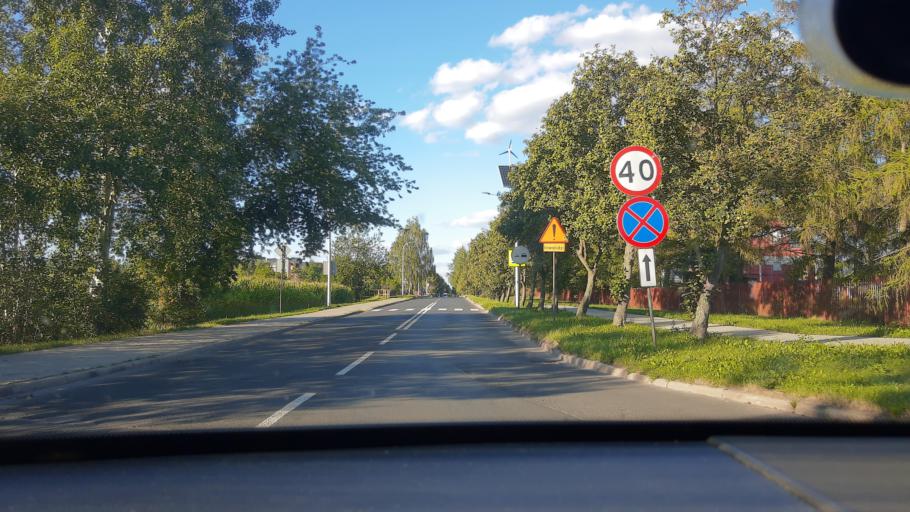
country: PL
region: Lodz Voivodeship
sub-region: Powiat sieradzki
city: Sieradz
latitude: 51.5787
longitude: 18.7048
